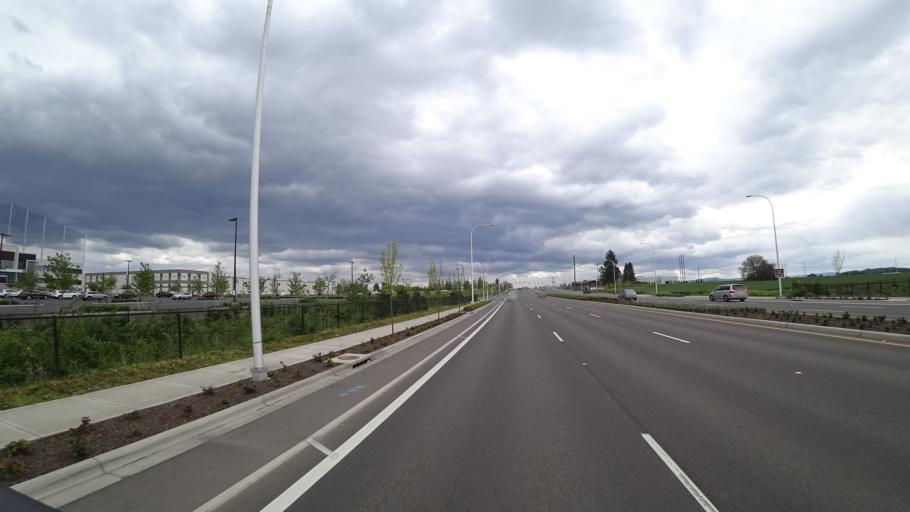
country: US
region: Oregon
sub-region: Washington County
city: Rockcreek
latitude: 45.5601
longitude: -122.9261
